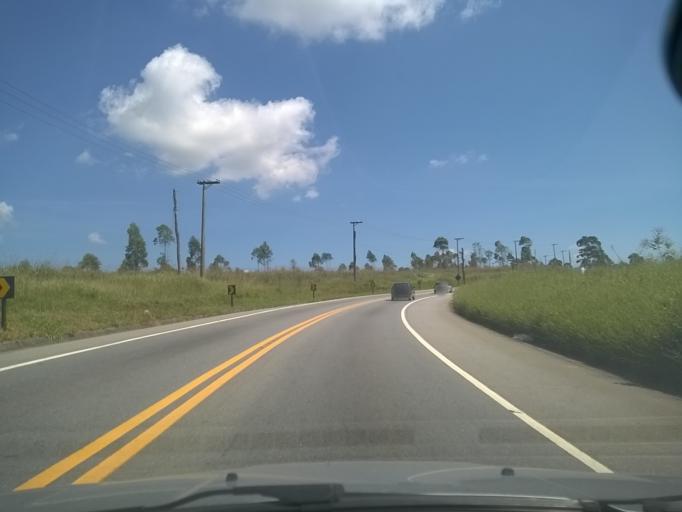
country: BR
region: Sao Paulo
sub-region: Francisco Morato
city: Francisco Morato
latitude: -23.2959
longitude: -46.7715
